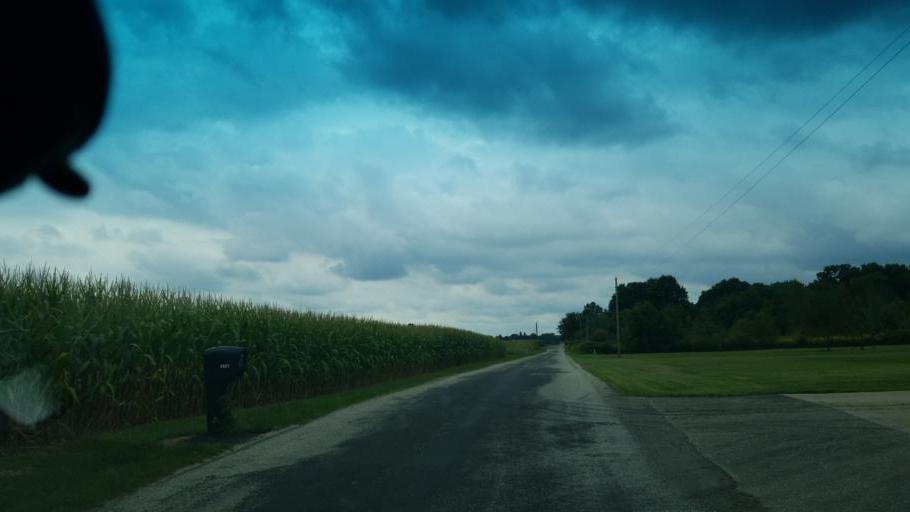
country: US
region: Ohio
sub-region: Richland County
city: Shelby
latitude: 40.8891
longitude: -82.5714
